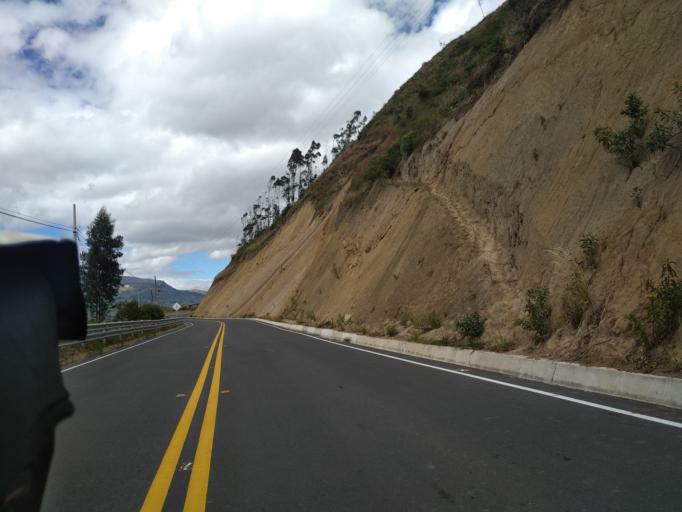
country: EC
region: Cotopaxi
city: Saquisili
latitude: -0.7088
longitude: -78.8824
